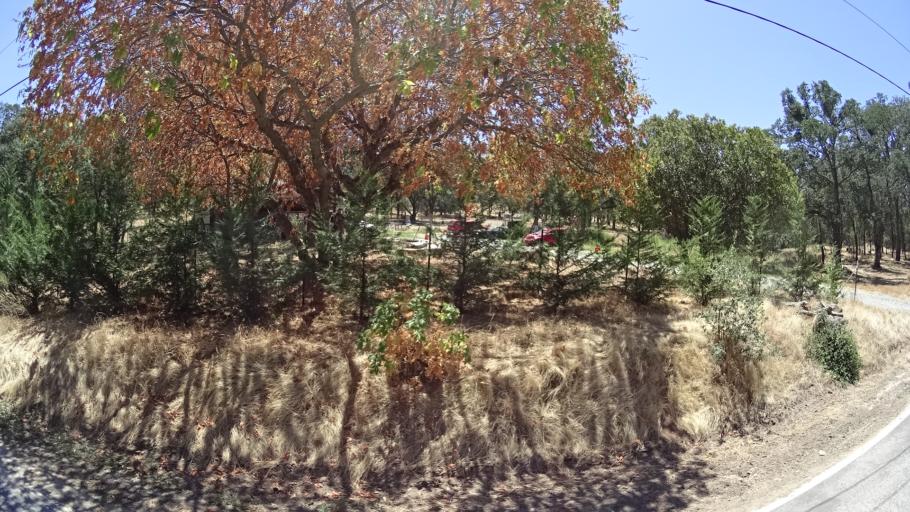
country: US
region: California
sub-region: Calaveras County
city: Rancho Calaveras
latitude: 38.1422
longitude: -120.8691
